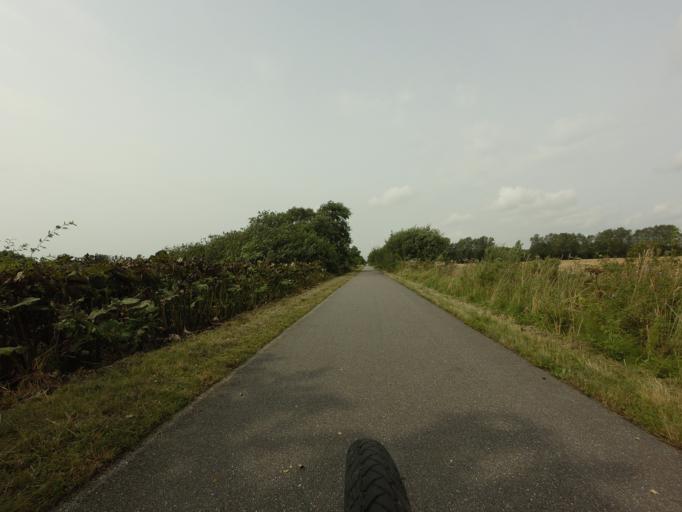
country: DK
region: Zealand
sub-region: Naestved Kommune
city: Fuglebjerg
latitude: 55.2575
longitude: 11.6371
